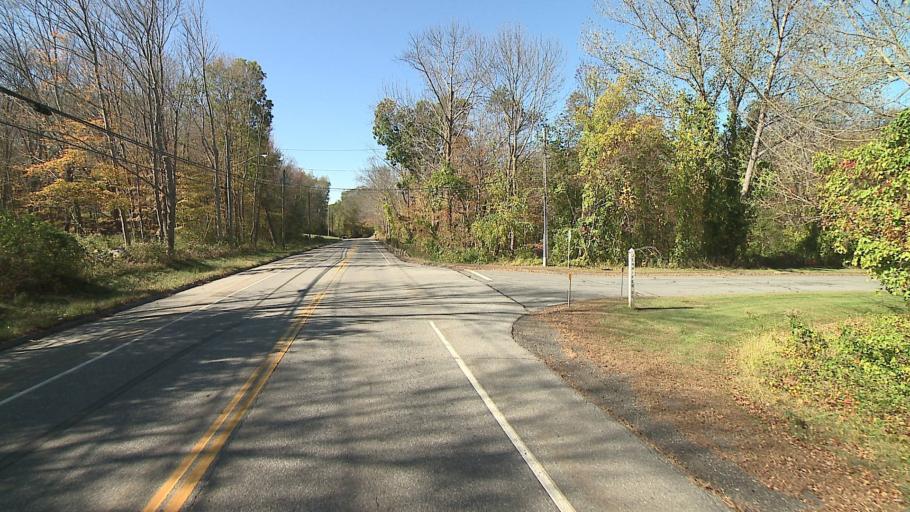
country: US
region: Connecticut
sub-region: Tolland County
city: Hebron
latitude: 41.6510
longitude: -72.3933
